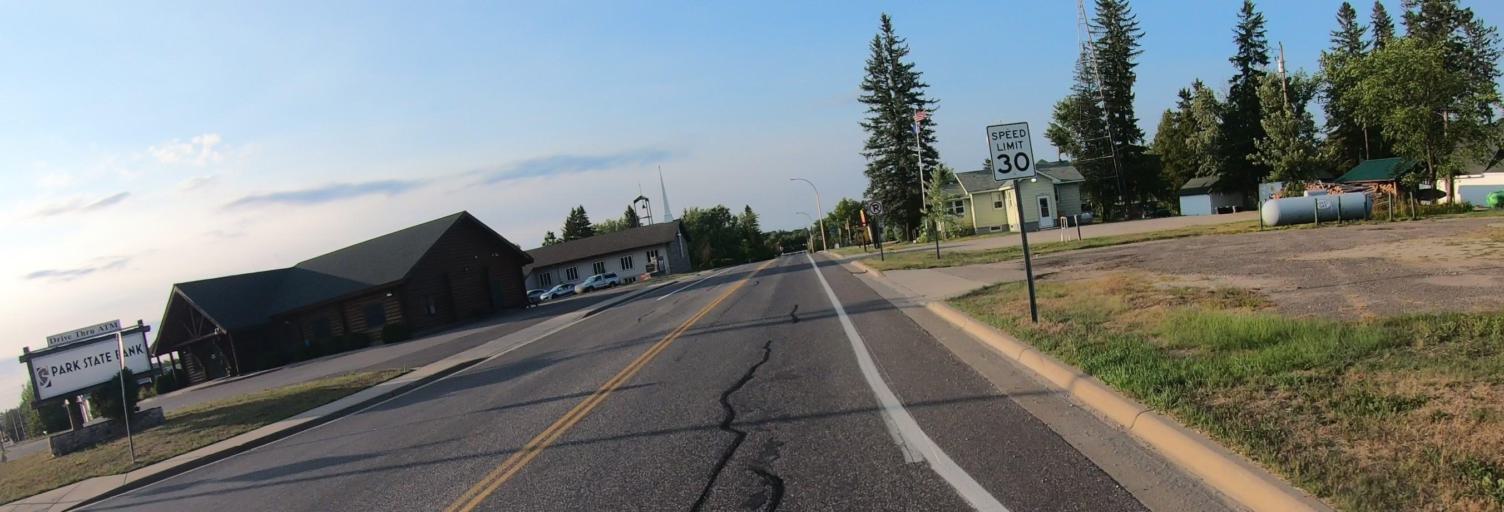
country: US
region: Minnesota
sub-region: Saint Louis County
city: Mountain Iron
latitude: 47.8469
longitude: -92.6804
